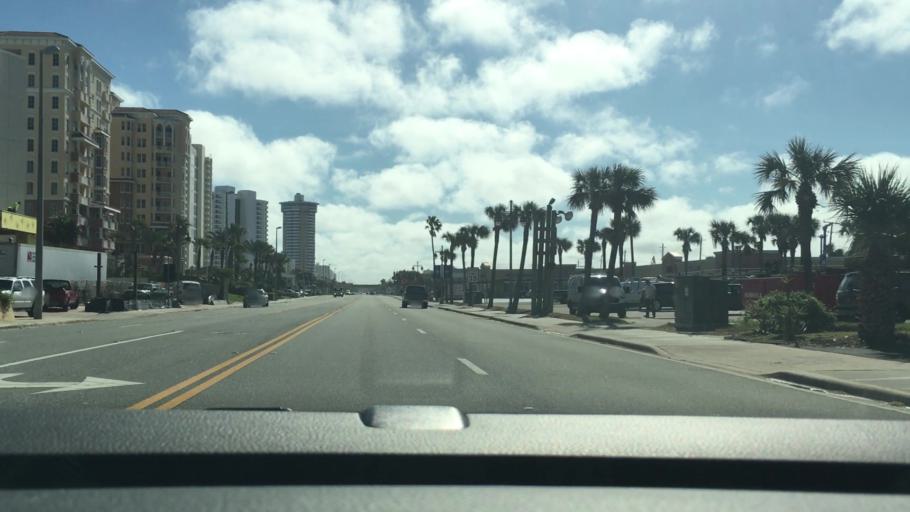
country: US
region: Florida
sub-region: Volusia County
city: Daytona Beach Shores
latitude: 29.1881
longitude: -80.9890
